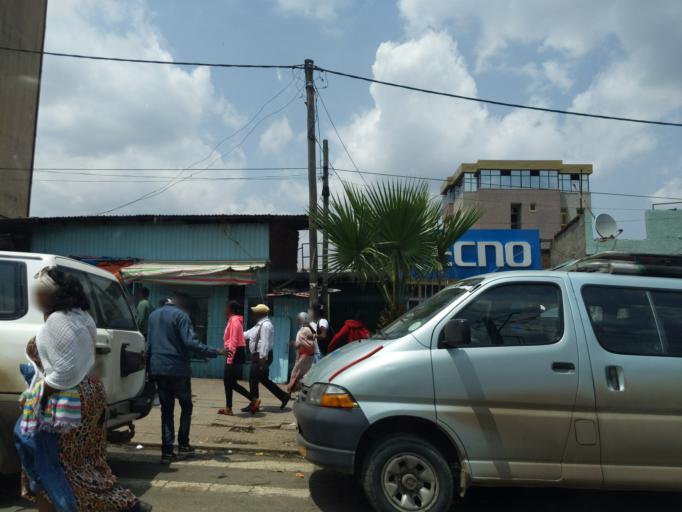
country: ET
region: Adis Abeba
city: Addis Ababa
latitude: 8.9557
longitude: 38.7638
